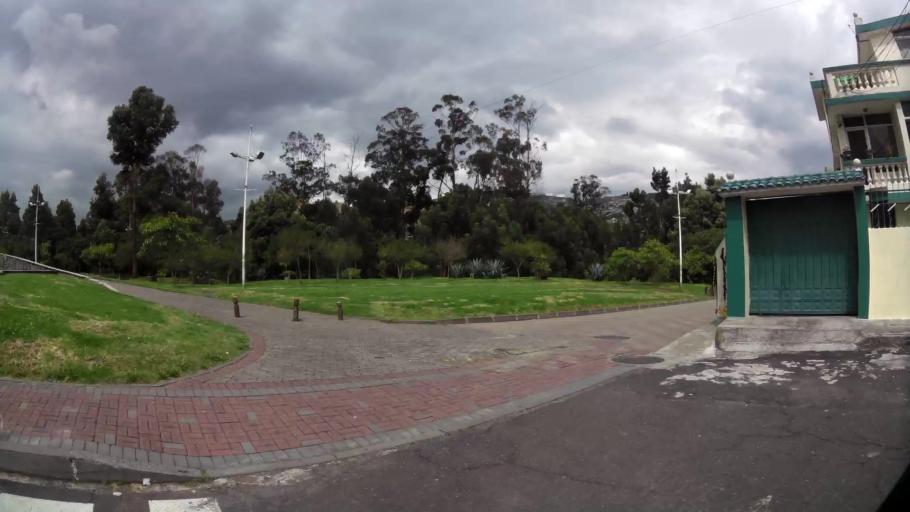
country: EC
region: Pichincha
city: Quito
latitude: -0.2520
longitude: -78.5266
